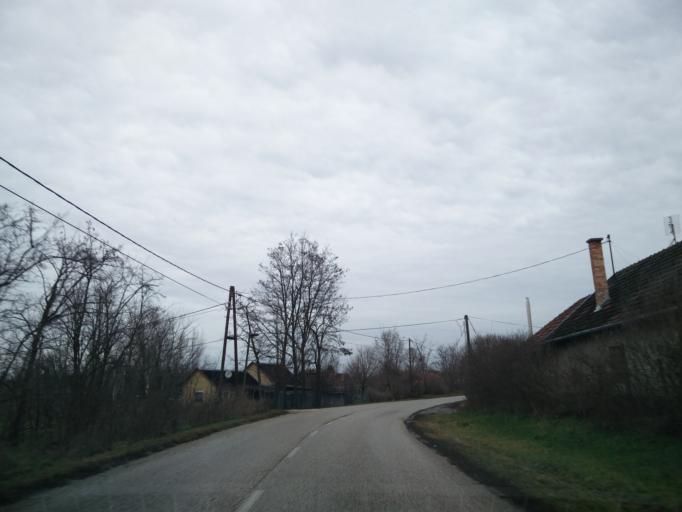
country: HU
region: Pest
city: Koka
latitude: 47.4751
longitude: 19.5645
